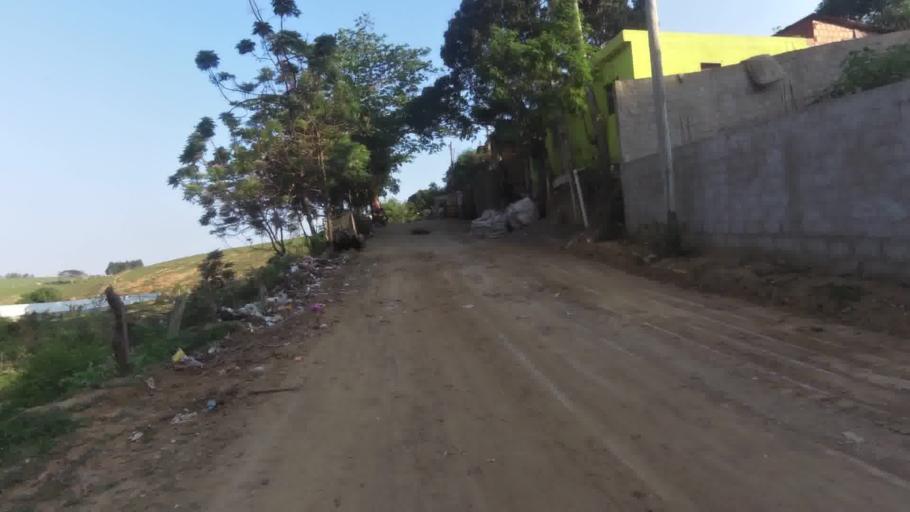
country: BR
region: Espirito Santo
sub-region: Piuma
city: Piuma
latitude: -20.8249
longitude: -40.7187
